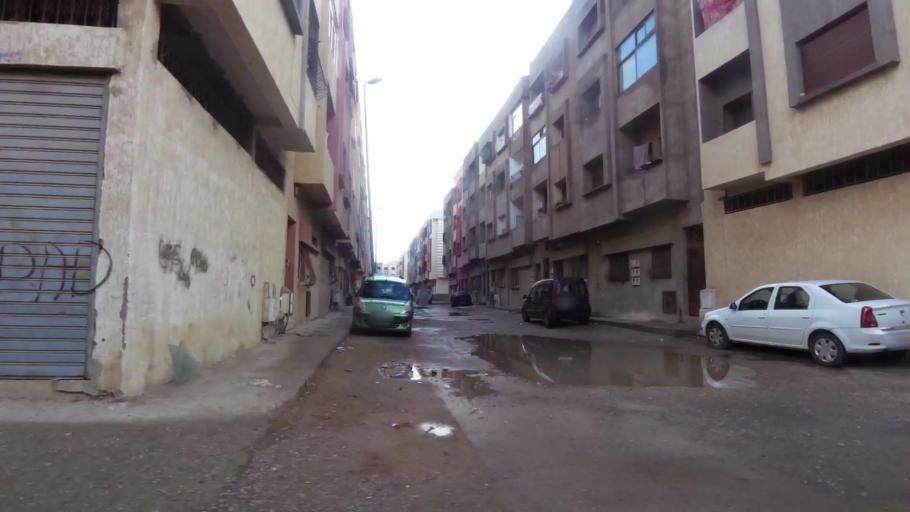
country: MA
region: Grand Casablanca
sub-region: Nouaceur
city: Bouskoura
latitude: 33.5356
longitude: -7.7052
